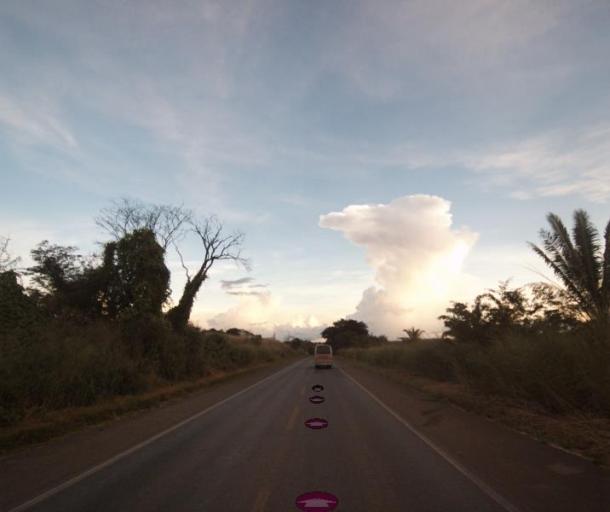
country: BR
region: Goias
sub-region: Uruacu
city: Uruacu
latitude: -14.4071
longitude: -49.1575
